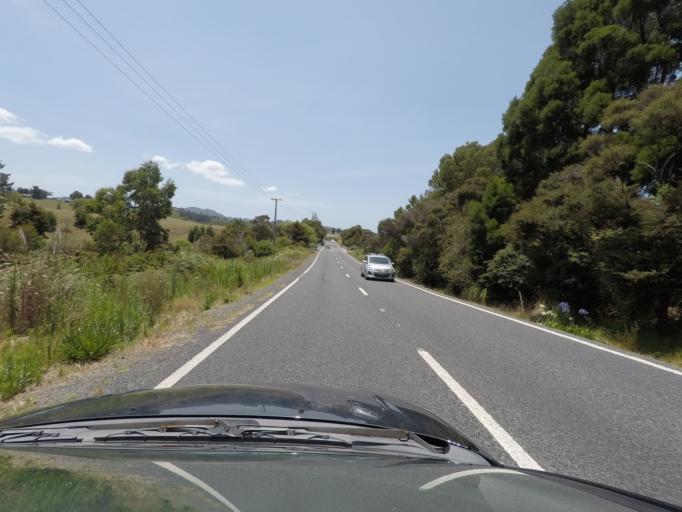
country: NZ
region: Auckland
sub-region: Auckland
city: Warkworth
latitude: -36.3697
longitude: 174.7058
